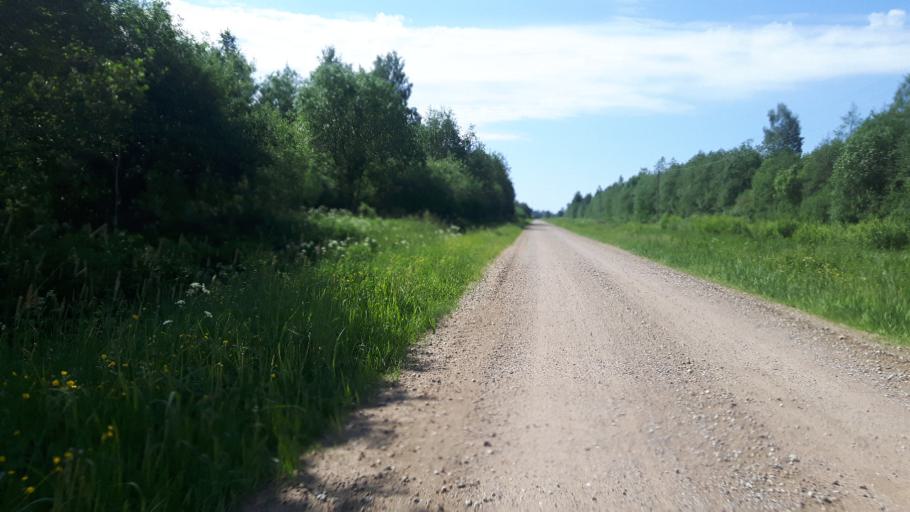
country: EE
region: Paernumaa
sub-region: Vaendra vald (alev)
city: Vandra
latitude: 58.6832
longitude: 25.0340
